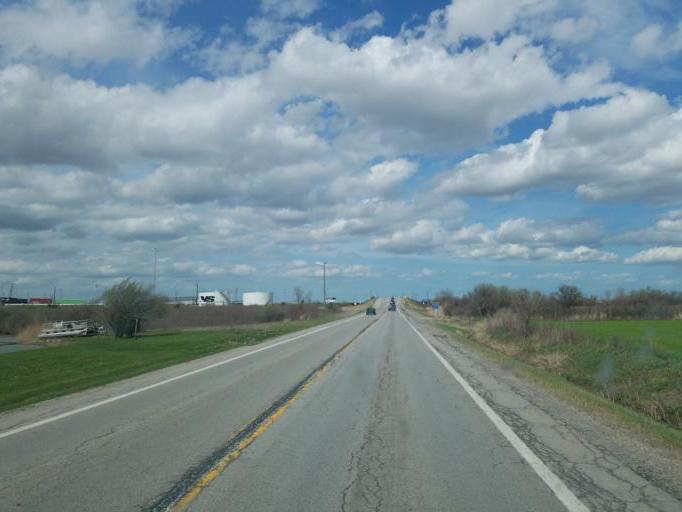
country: US
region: Ohio
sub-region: Huron County
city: Bellevue
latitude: 41.2889
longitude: -82.7838
